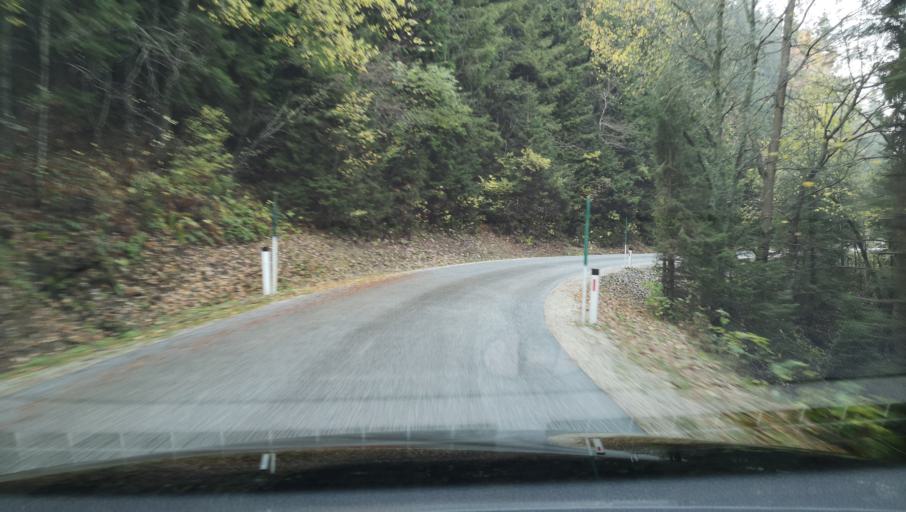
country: AT
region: Styria
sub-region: Politischer Bezirk Weiz
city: Gasen
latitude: 47.3560
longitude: 15.5888
